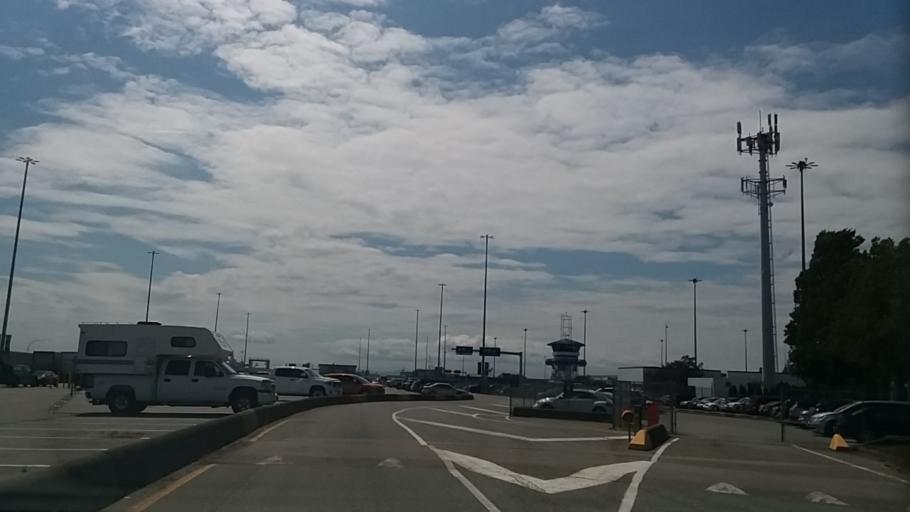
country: US
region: Washington
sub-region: Whatcom County
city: Point Roberts
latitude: 49.0104
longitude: -123.1244
